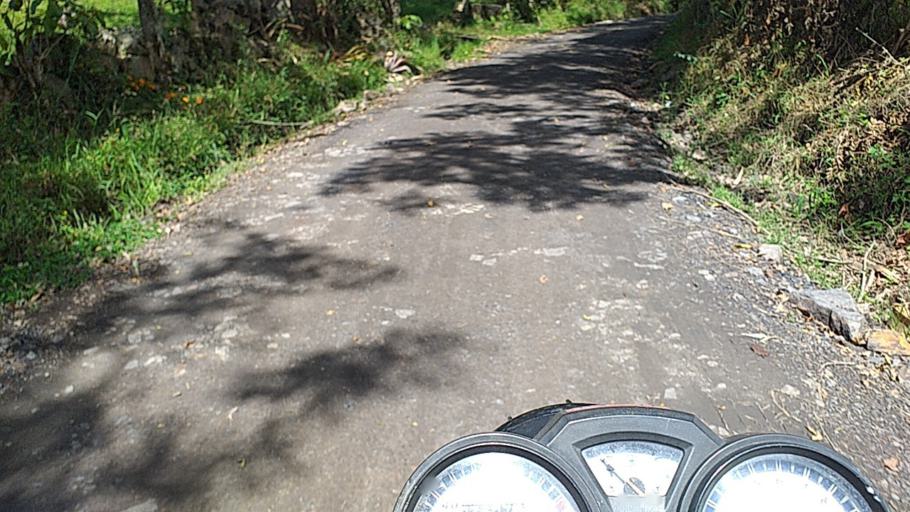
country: CO
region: Cundinamarca
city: Tenza
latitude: 5.1084
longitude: -73.4519
